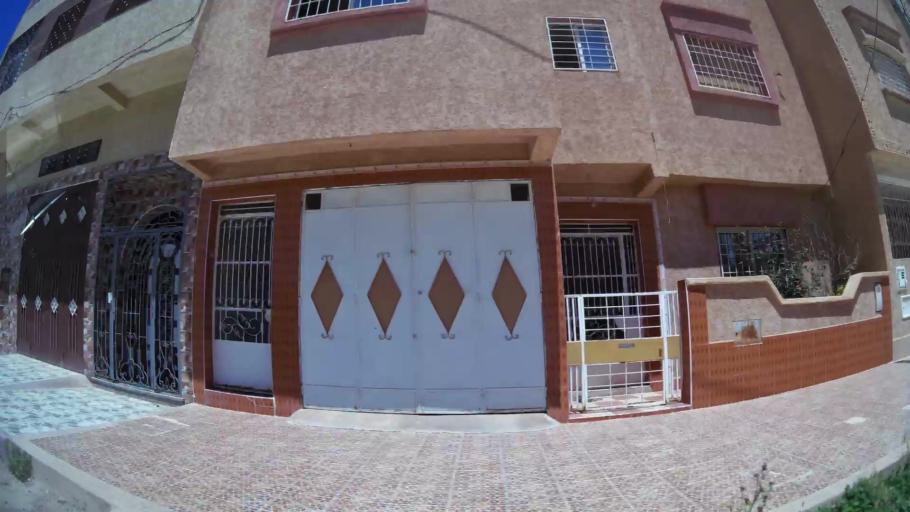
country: MA
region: Oriental
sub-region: Oujda-Angad
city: Oujda
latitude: 34.6666
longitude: -1.8819
